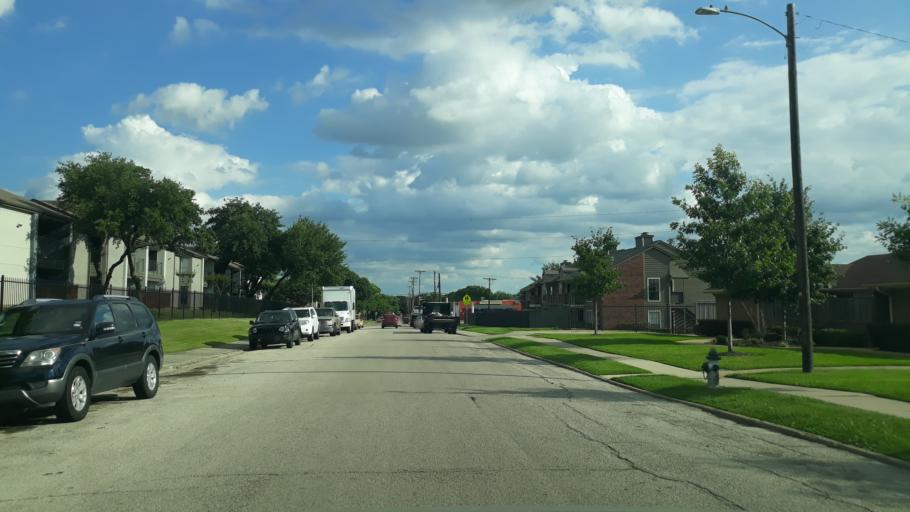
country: US
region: Texas
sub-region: Dallas County
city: Irving
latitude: 32.8584
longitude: -97.0050
